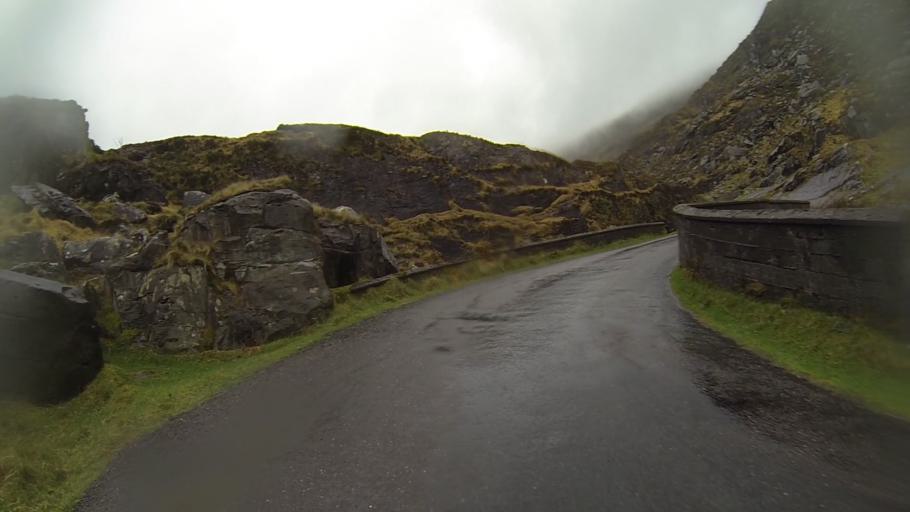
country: IE
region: Munster
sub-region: Ciarrai
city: Kenmare
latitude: 52.0029
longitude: -9.6427
